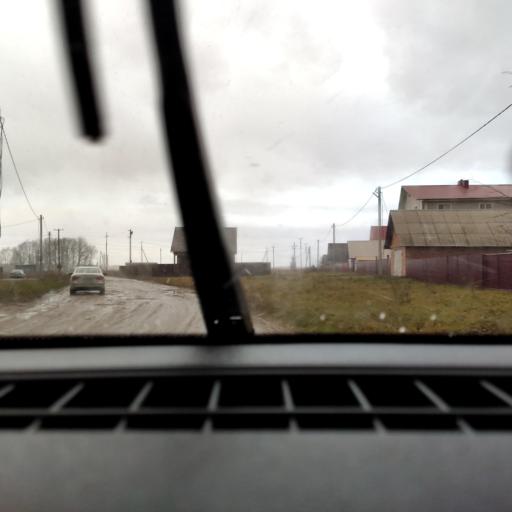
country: RU
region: Bashkortostan
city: Iglino
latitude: 54.7368
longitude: 56.3258
